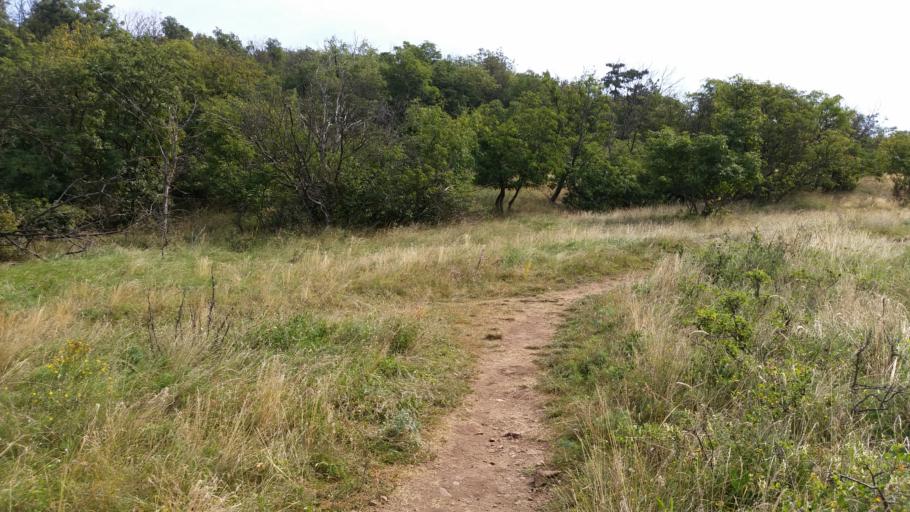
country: HU
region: Veszprem
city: Tihany
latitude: 46.9122
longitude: 17.8543
